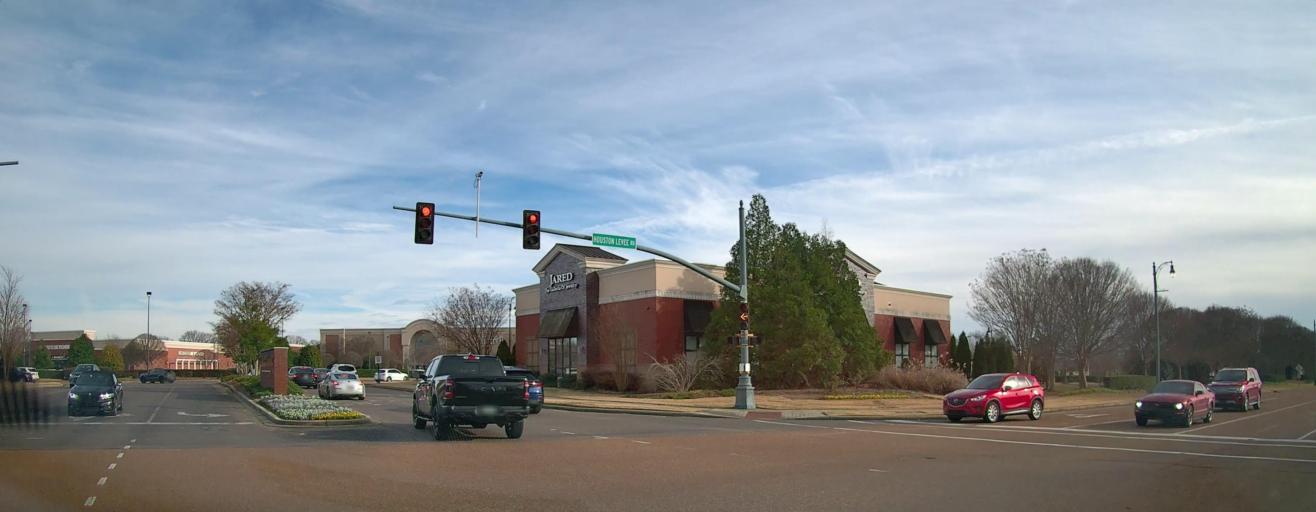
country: US
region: Tennessee
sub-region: Shelby County
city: Collierville
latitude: 35.0226
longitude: -89.7227
